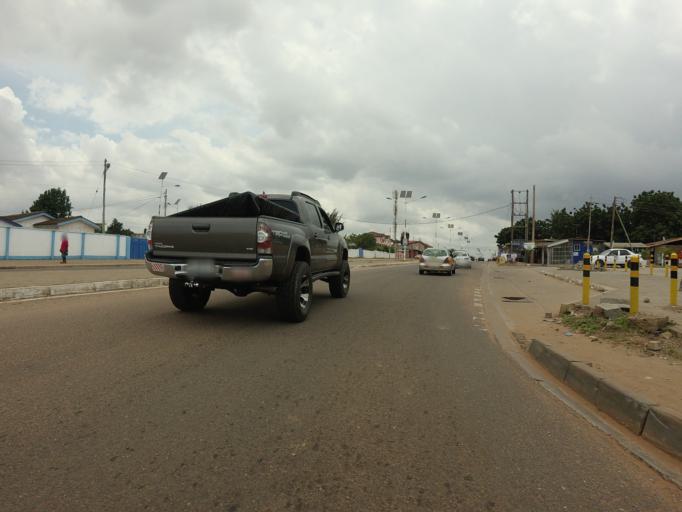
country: GH
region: Greater Accra
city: Medina Estates
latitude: 5.6602
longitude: -0.1514
